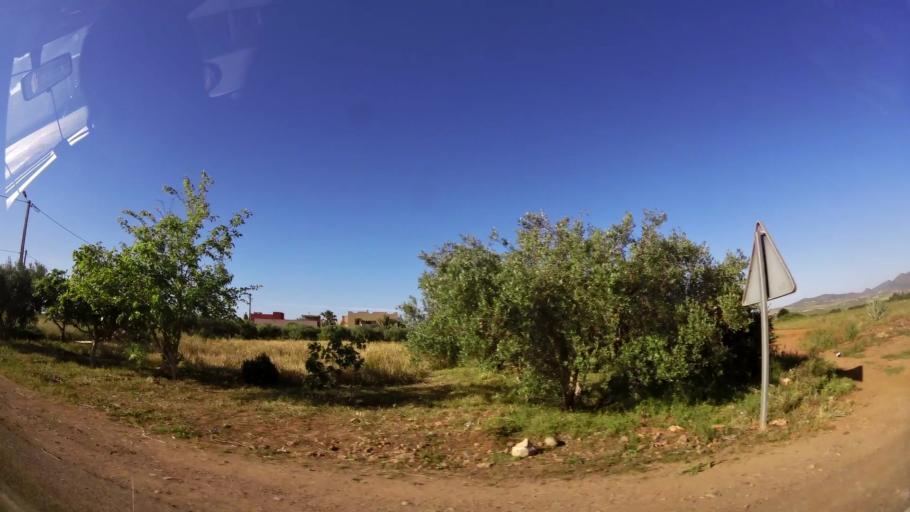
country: MA
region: Oriental
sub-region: Berkane-Taourirt
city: Ahfir
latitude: 35.0072
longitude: -2.1885
